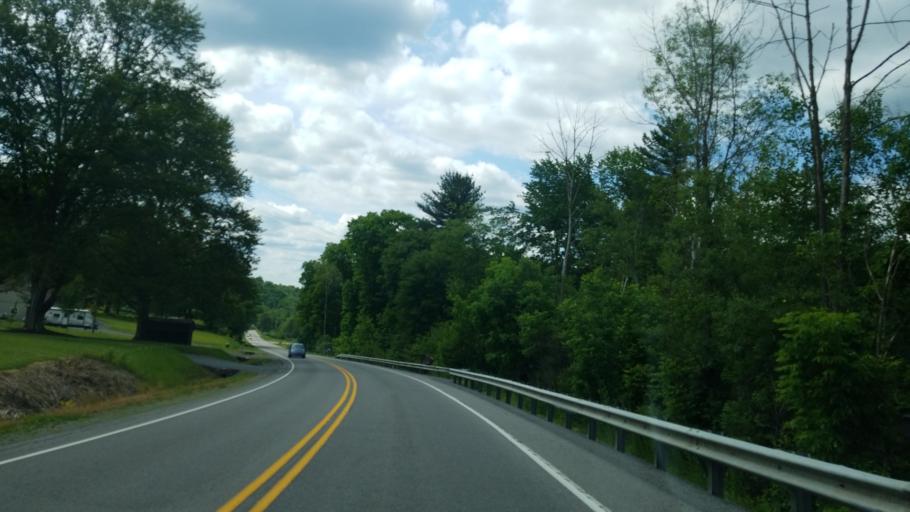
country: US
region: Pennsylvania
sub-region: Clearfield County
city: Clearfield
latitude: 40.9726
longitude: -78.3786
